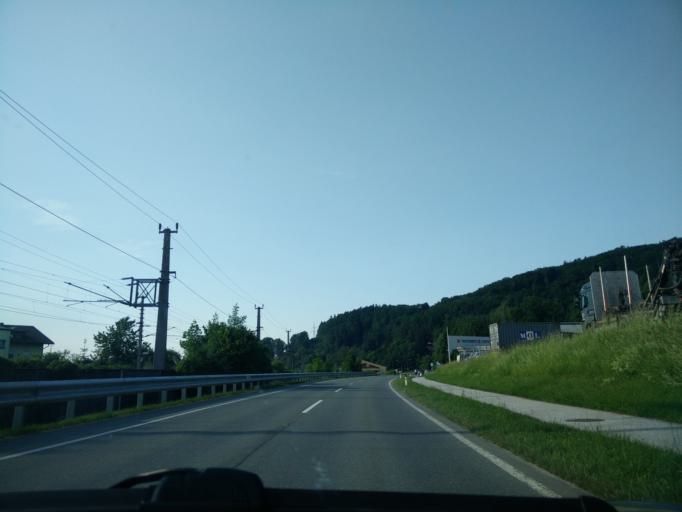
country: AT
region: Salzburg
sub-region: Politischer Bezirk Salzburg-Umgebung
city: Elsbethen
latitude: 47.7335
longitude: 13.0886
